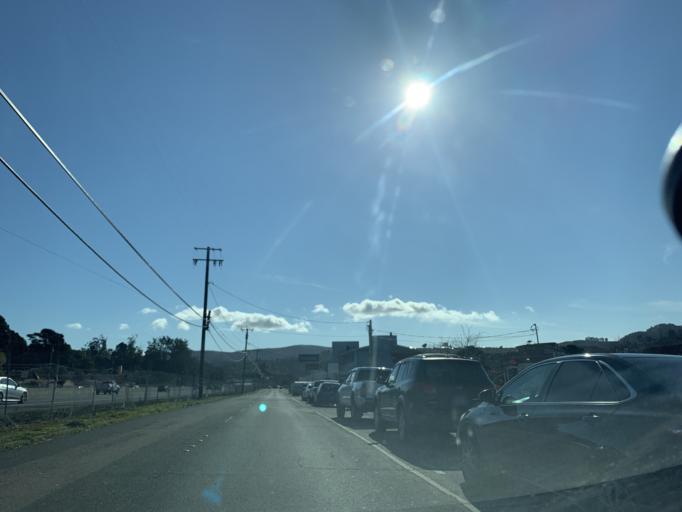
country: US
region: California
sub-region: Marin County
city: Strawberry
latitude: 37.8944
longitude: -122.5167
